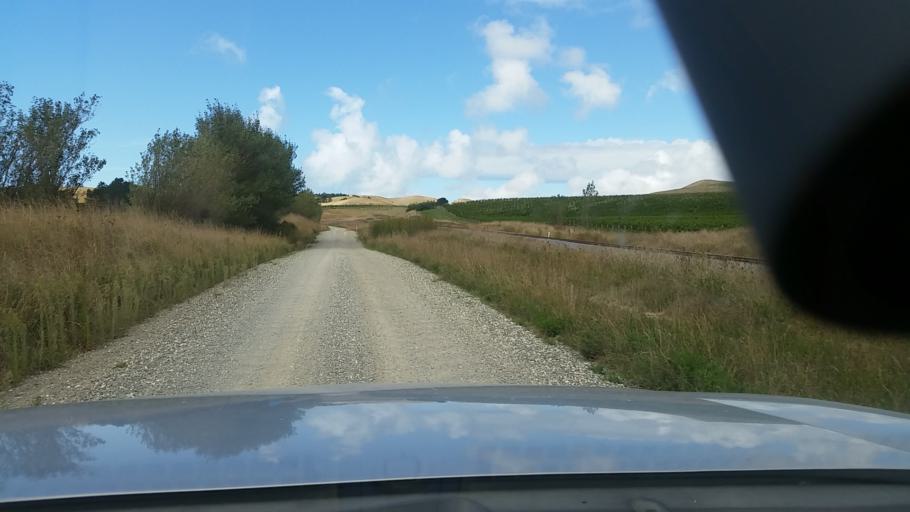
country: NZ
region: Marlborough
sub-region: Marlborough District
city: Blenheim
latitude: -41.6877
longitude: 174.1345
